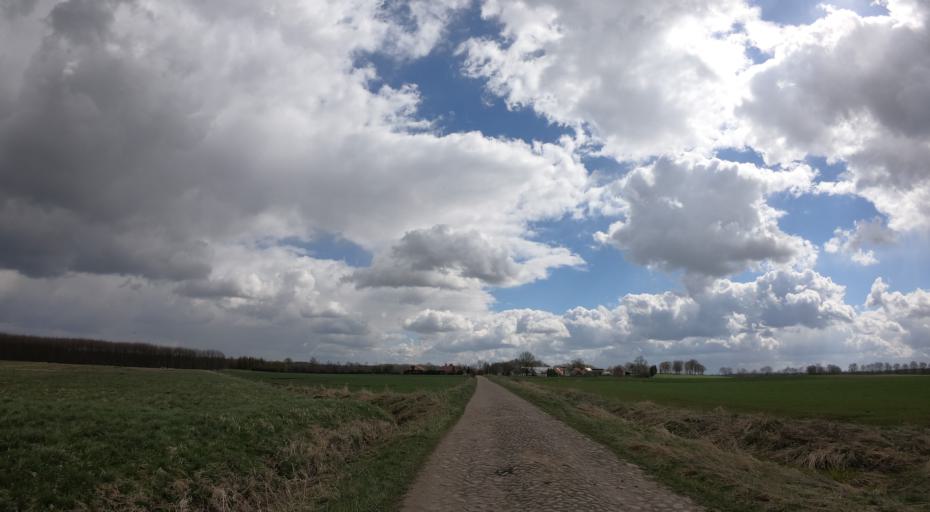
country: PL
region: West Pomeranian Voivodeship
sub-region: Powiat drawski
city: Drawsko Pomorskie
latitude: 53.5438
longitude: 15.8658
